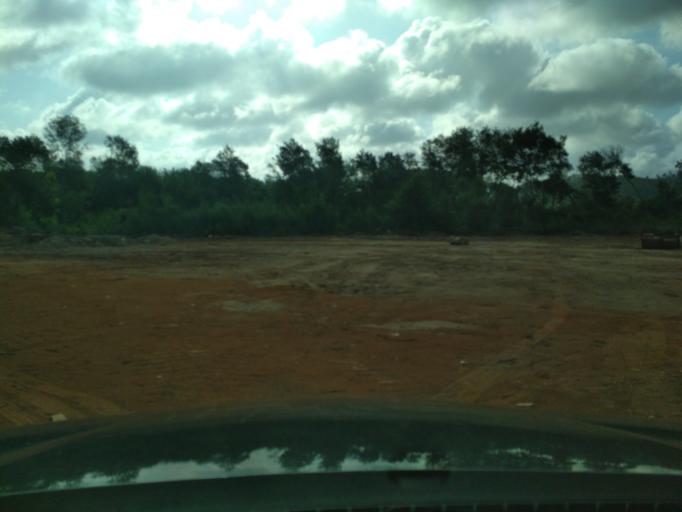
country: PT
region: Coimbra
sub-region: Coimbra
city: Coimbra
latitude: 40.1800
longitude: -8.4165
